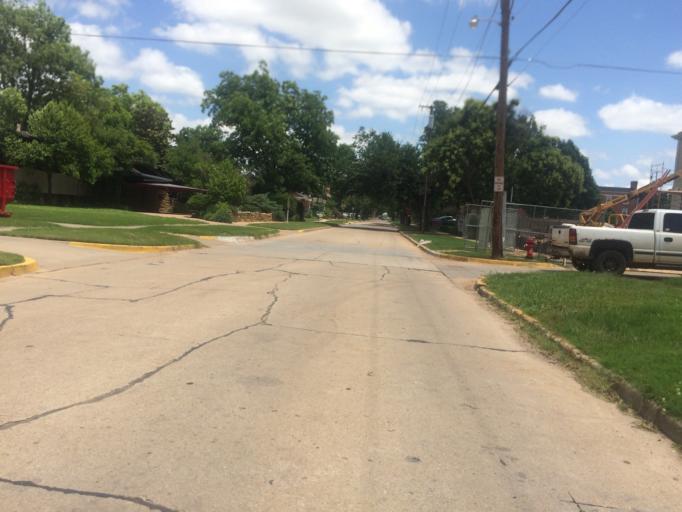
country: US
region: Oklahoma
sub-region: Cleveland County
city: Norman
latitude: 35.2075
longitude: -97.4512
